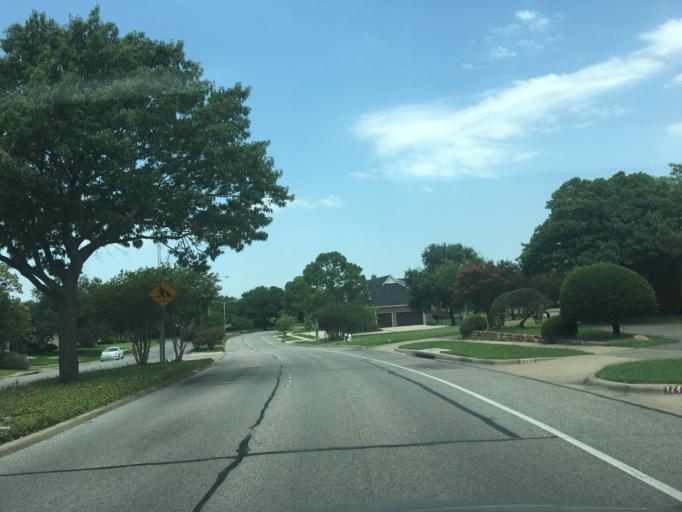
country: US
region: Texas
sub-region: Dallas County
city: Carrollton
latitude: 32.9359
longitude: -96.8681
